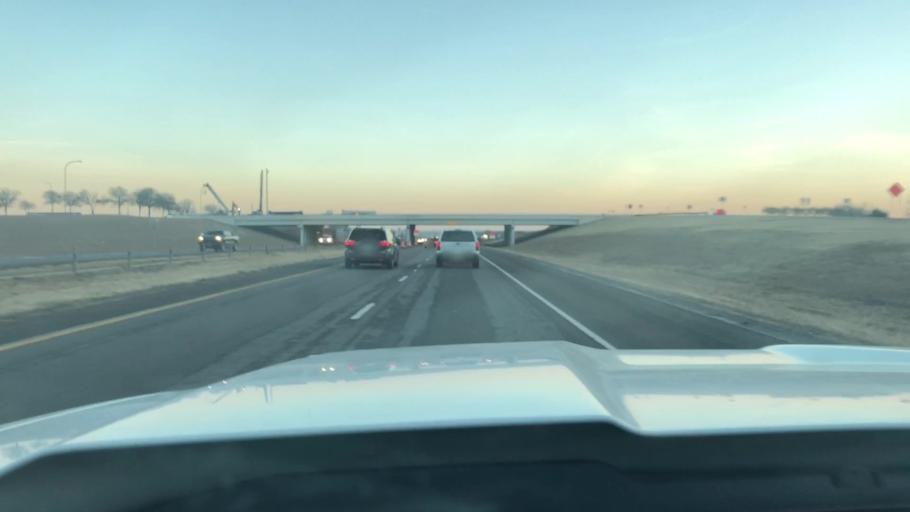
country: US
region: Texas
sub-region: Tarrant County
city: Haslet
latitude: 32.9984
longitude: -97.2944
